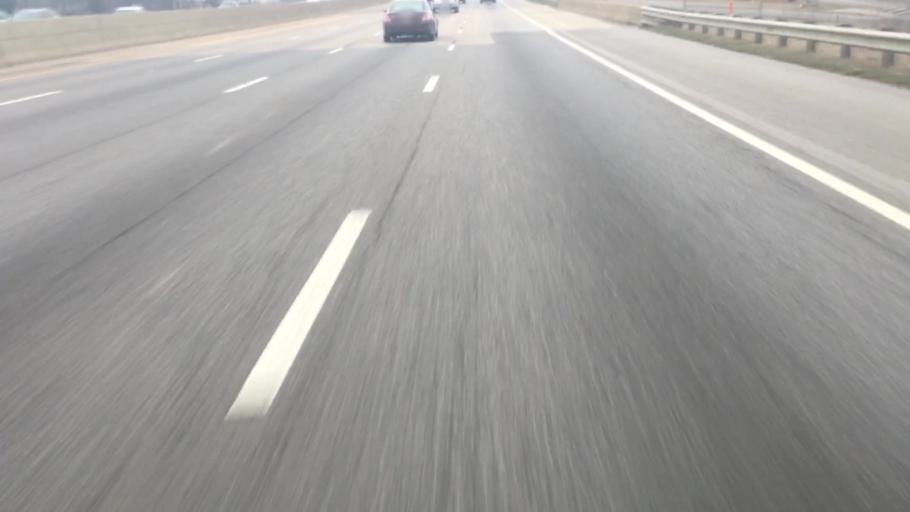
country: US
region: Alabama
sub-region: Jefferson County
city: Birmingham
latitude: 33.5509
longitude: -86.8299
